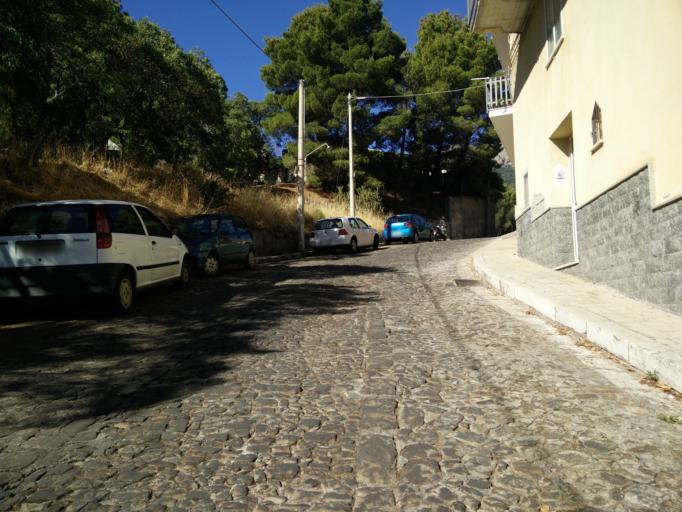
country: IT
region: Sicily
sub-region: Palermo
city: Castelbuono
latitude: 37.9263
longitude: 14.0886
